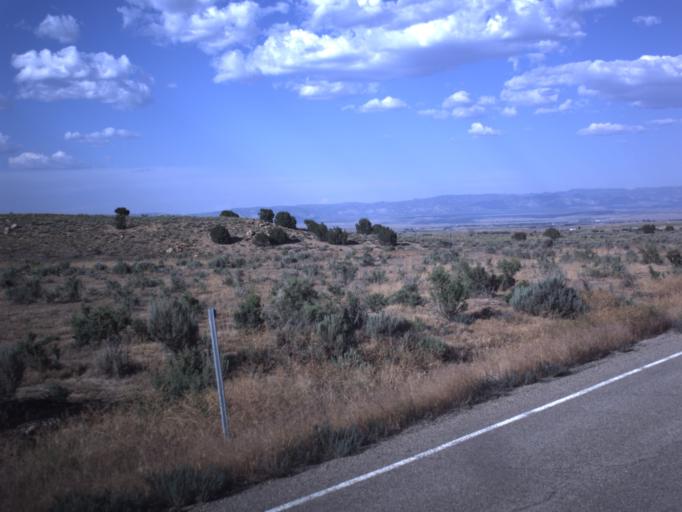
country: US
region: Utah
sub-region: Carbon County
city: Price
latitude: 39.4844
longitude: -110.9007
